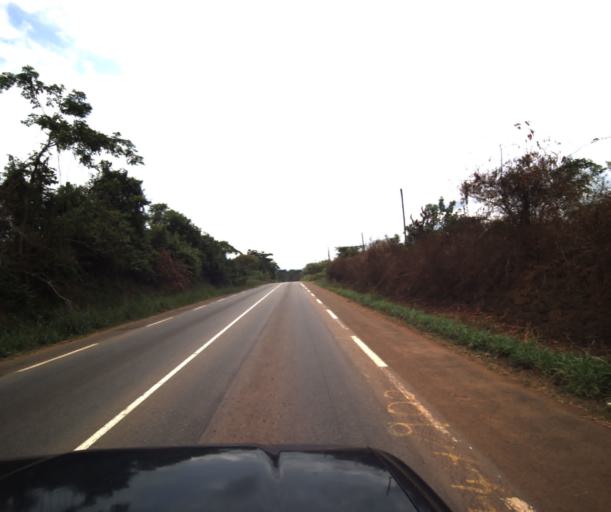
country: CM
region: Centre
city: Eseka
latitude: 3.8657
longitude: 10.9208
